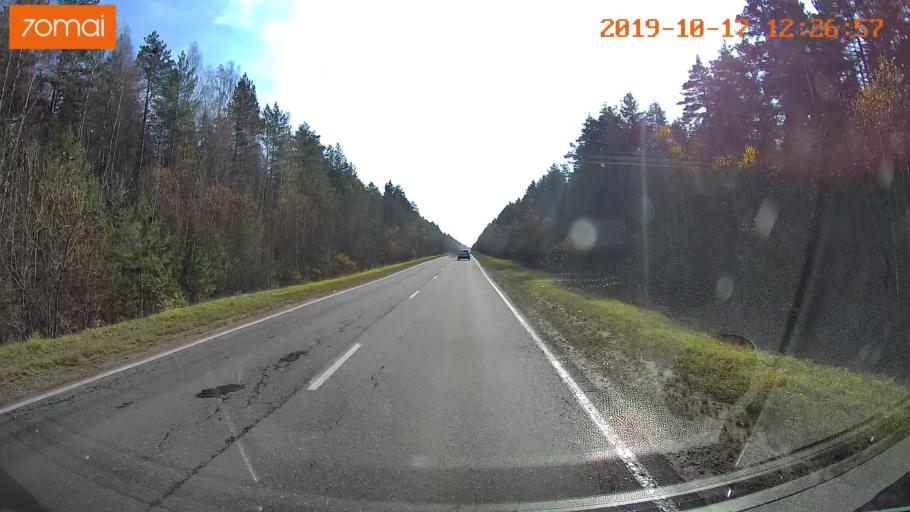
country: RU
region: Rjazan
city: Syntul
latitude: 55.0120
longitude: 41.2595
